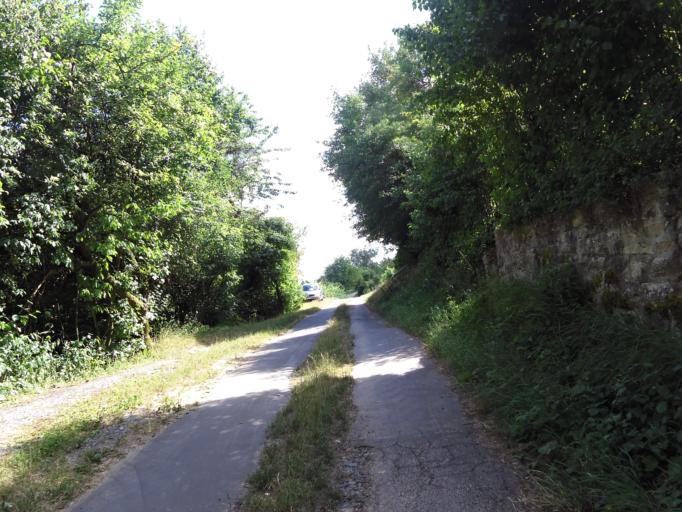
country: DE
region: Bavaria
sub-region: Regierungsbezirk Unterfranken
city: Randersacker
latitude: 49.7505
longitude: 9.9675
